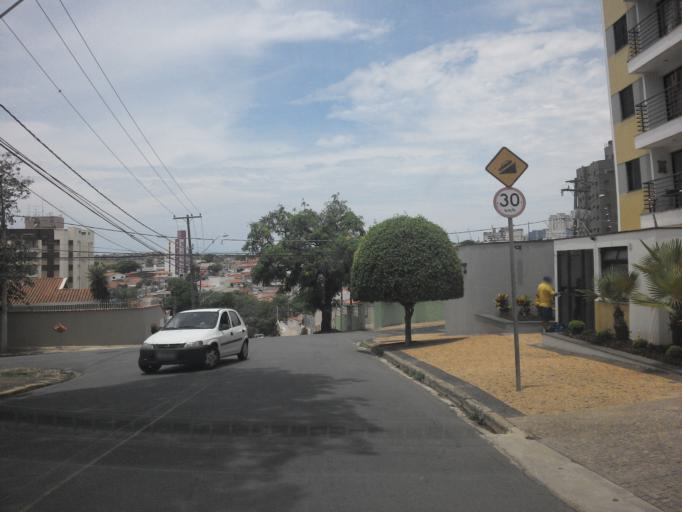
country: BR
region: Sao Paulo
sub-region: Campinas
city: Campinas
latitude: -22.9173
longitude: -47.0455
